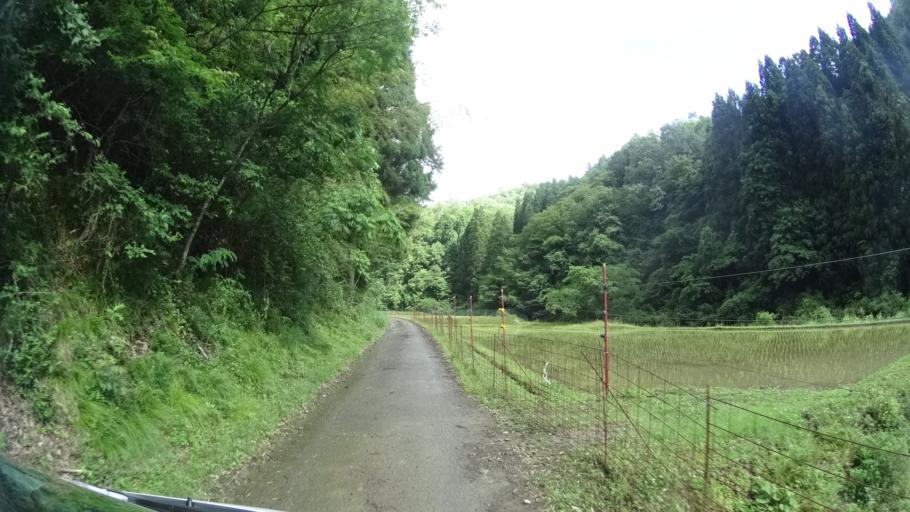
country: JP
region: Kyoto
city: Maizuru
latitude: 35.3916
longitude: 135.2702
